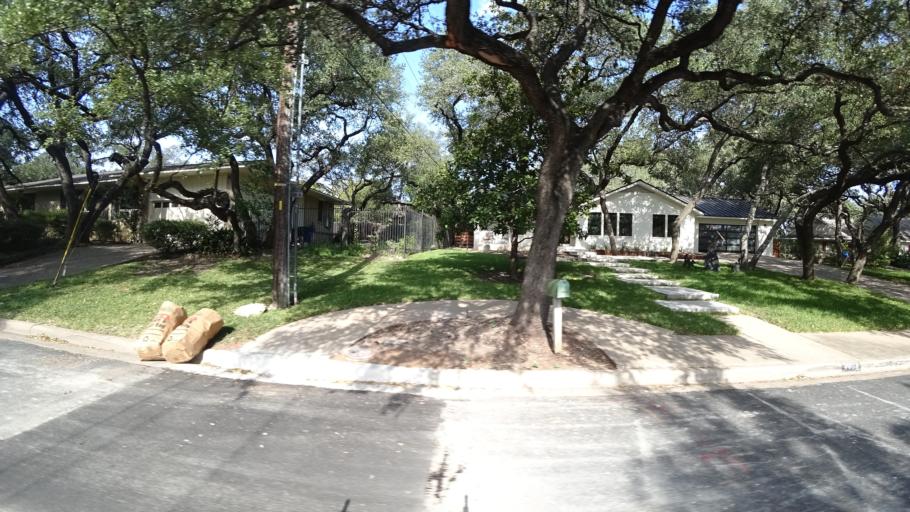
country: US
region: Texas
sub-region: Travis County
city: West Lake Hills
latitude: 30.3420
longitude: -97.7562
